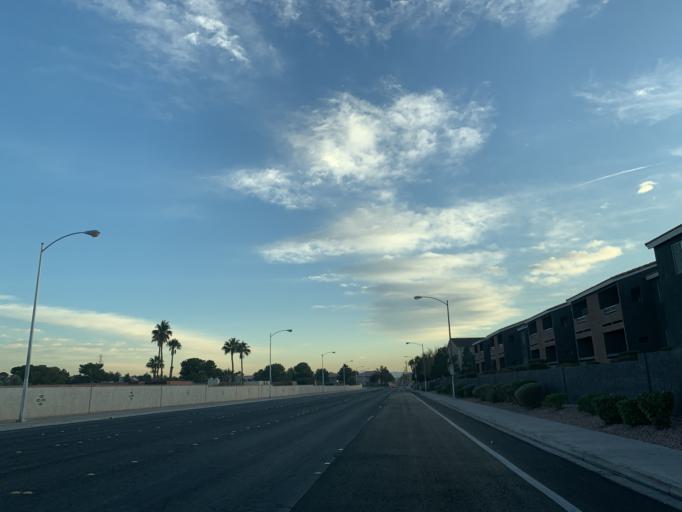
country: US
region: Nevada
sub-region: Clark County
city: Spring Valley
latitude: 36.1105
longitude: -115.2166
